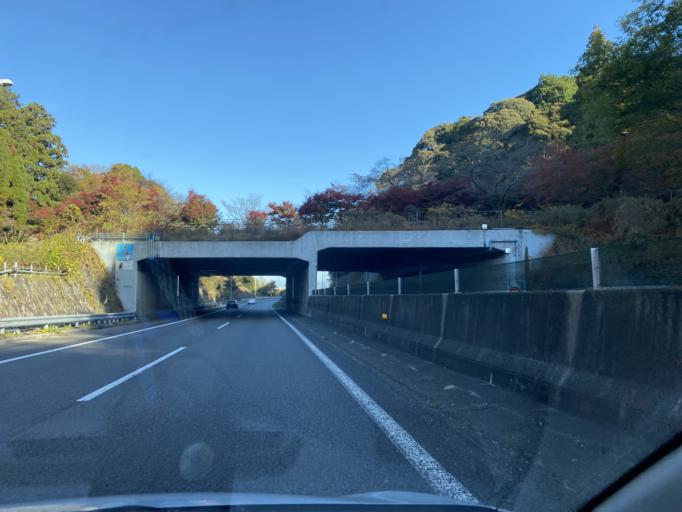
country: JP
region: Shiga Prefecture
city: Hikone
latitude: 35.1837
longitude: 136.2819
